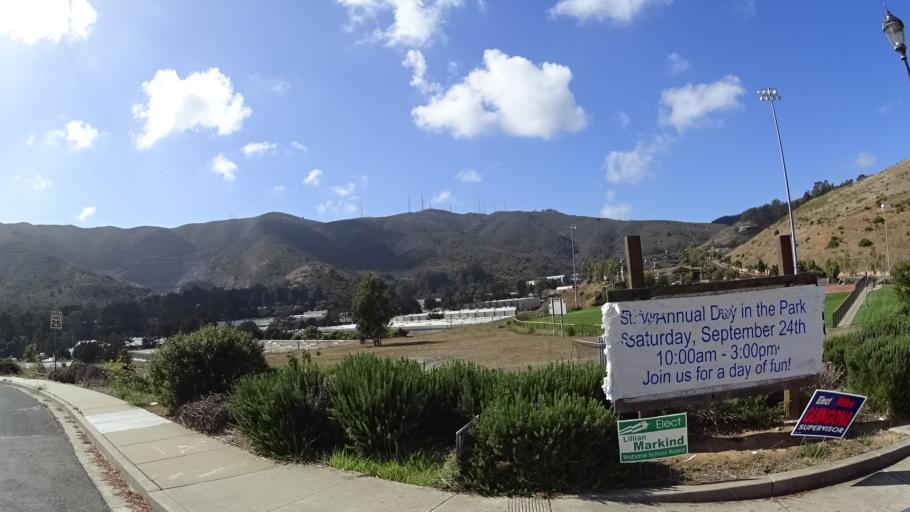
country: US
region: California
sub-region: San Mateo County
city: Brisbane
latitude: 37.6922
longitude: -122.4123
